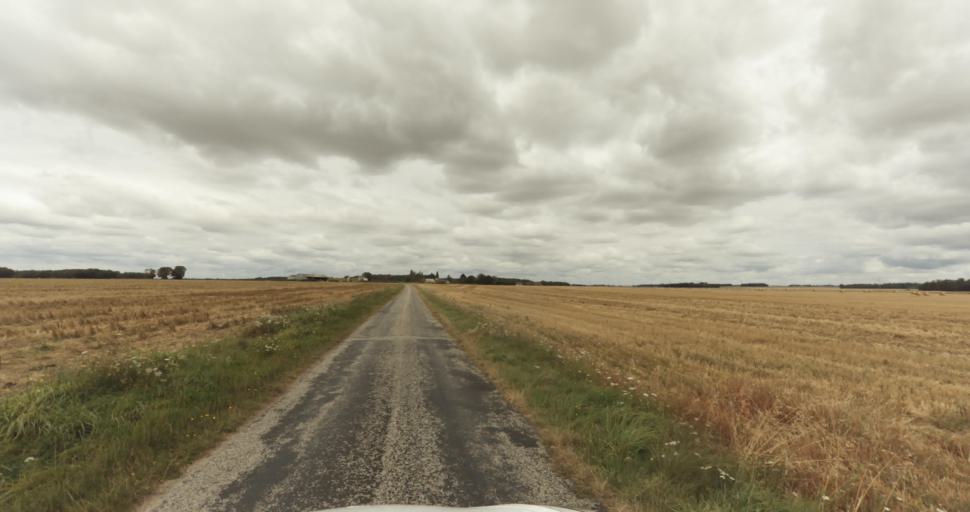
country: FR
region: Haute-Normandie
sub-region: Departement de l'Eure
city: Nonancourt
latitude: 48.7939
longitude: 1.1388
